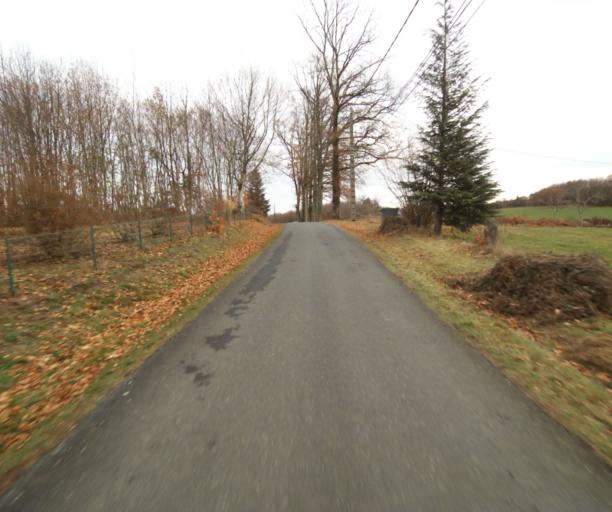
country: FR
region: Limousin
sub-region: Departement de la Correze
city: Chameyrat
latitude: 45.2357
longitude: 1.6788
